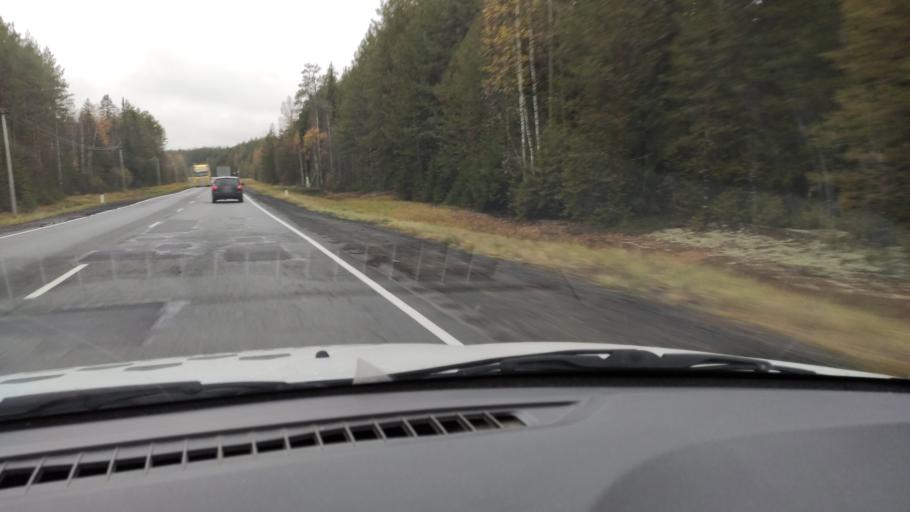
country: RU
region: Kirov
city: Belaya Kholunitsa
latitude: 58.9084
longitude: 50.9927
